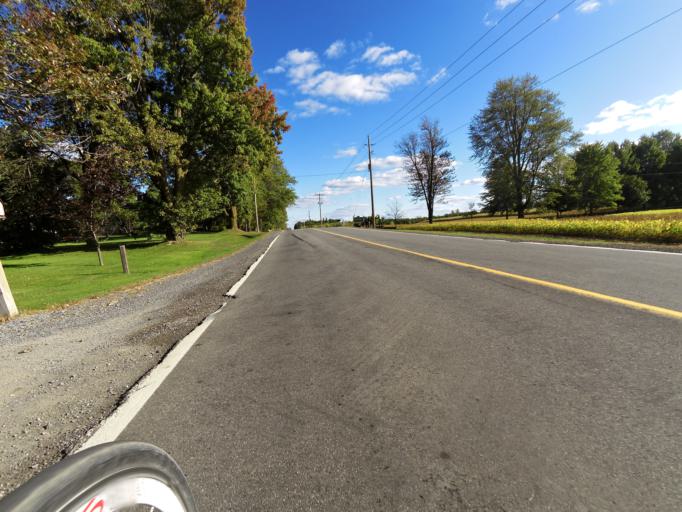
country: CA
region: Ontario
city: Bells Corners
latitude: 45.1143
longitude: -75.7289
